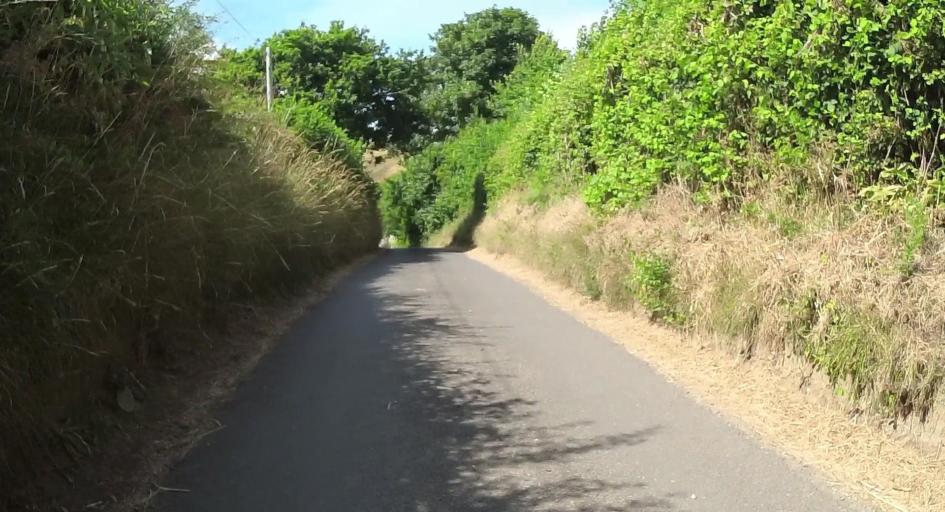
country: GB
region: England
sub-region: Dorset
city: Swanage
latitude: 50.6296
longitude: -2.0072
